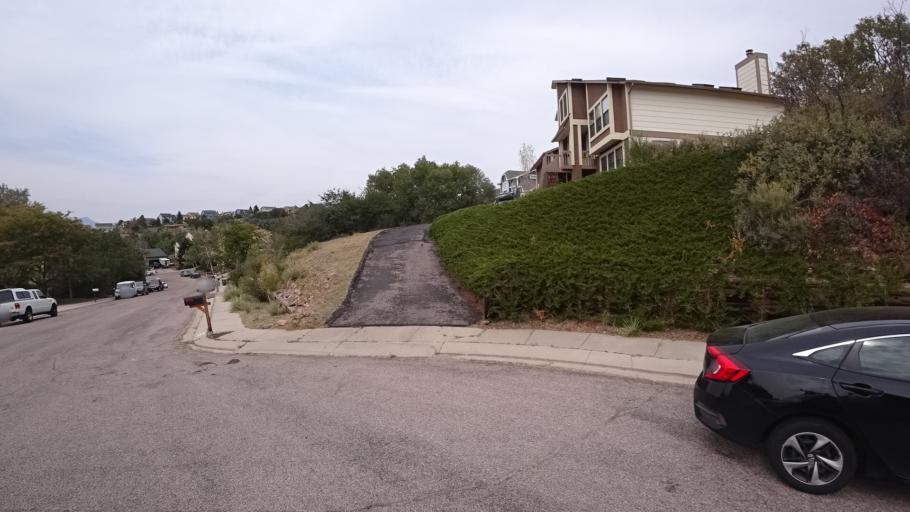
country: US
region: Colorado
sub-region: El Paso County
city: Cimarron Hills
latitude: 38.9071
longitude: -104.7249
